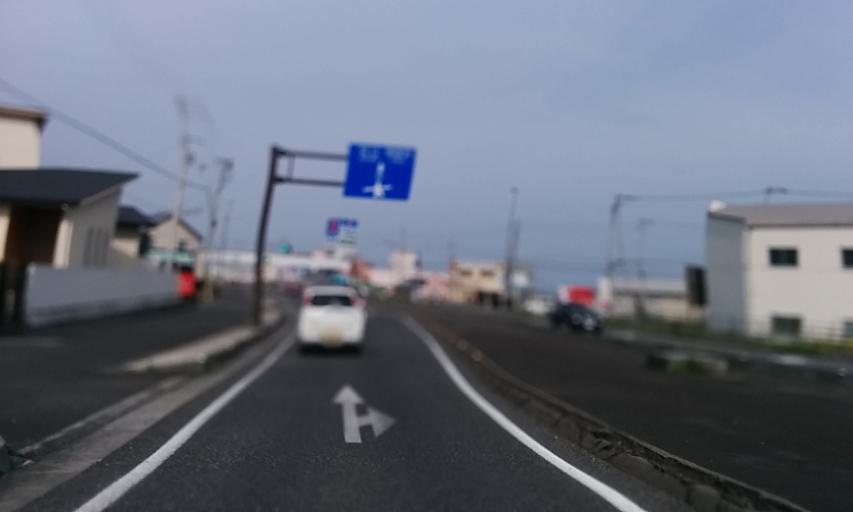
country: JP
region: Ehime
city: Kawanoecho
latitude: 33.9742
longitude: 133.5309
